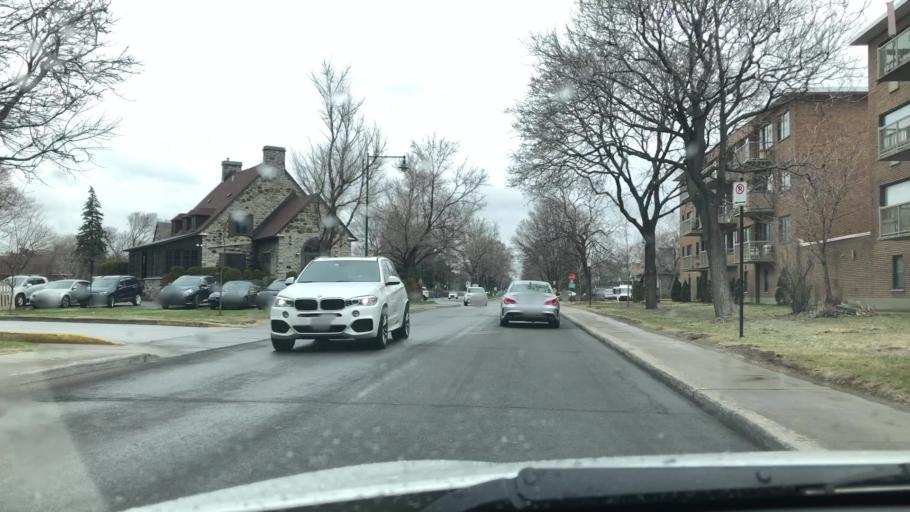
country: CA
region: Quebec
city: Saint-Laurent
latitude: 45.5085
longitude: -73.6613
